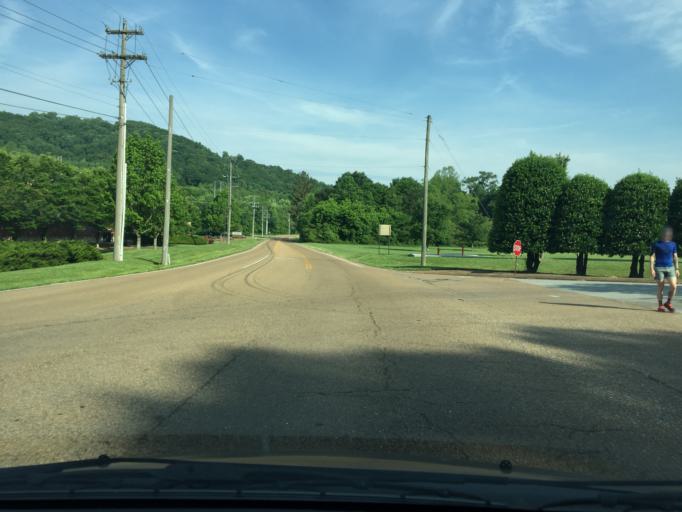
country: US
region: Tennessee
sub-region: Hamilton County
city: Apison
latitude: 35.0426
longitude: -85.0309
